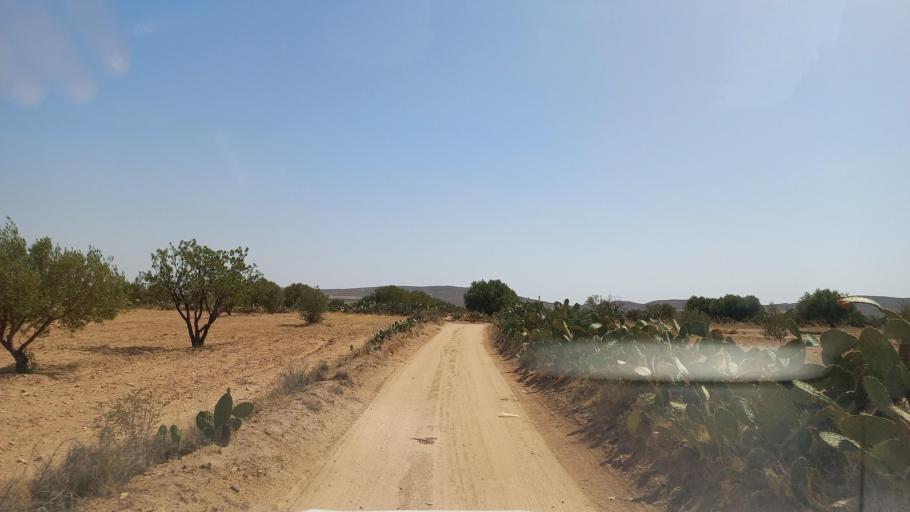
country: TN
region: Al Qasrayn
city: Kasserine
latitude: 35.2182
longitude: 9.0363
